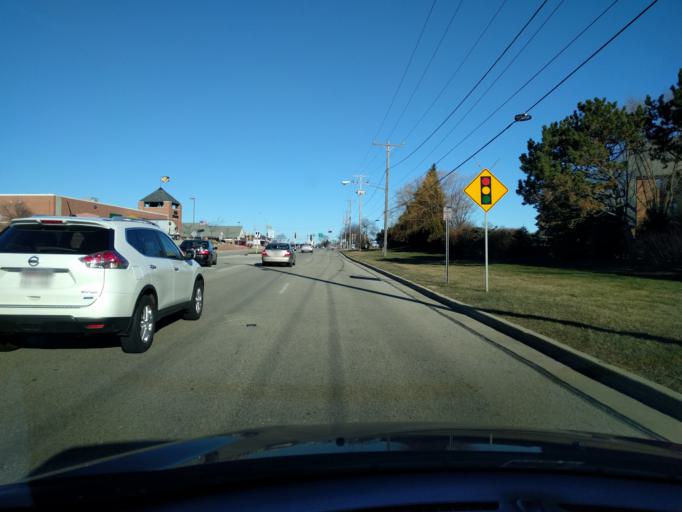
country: US
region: Wisconsin
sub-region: Milwaukee County
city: River Hills
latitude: 43.1736
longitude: -87.9125
